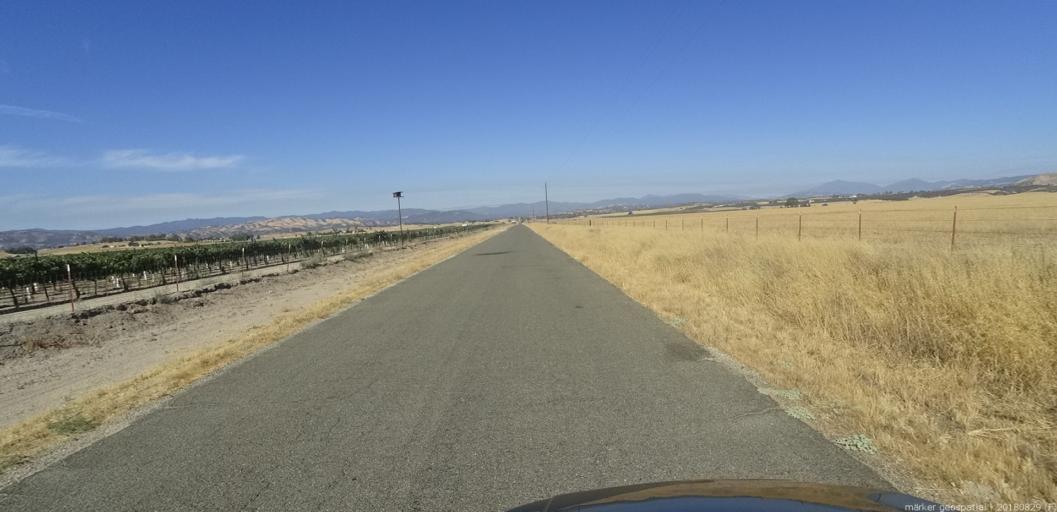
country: US
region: California
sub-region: Monterey County
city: King City
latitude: 35.9659
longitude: -121.0889
